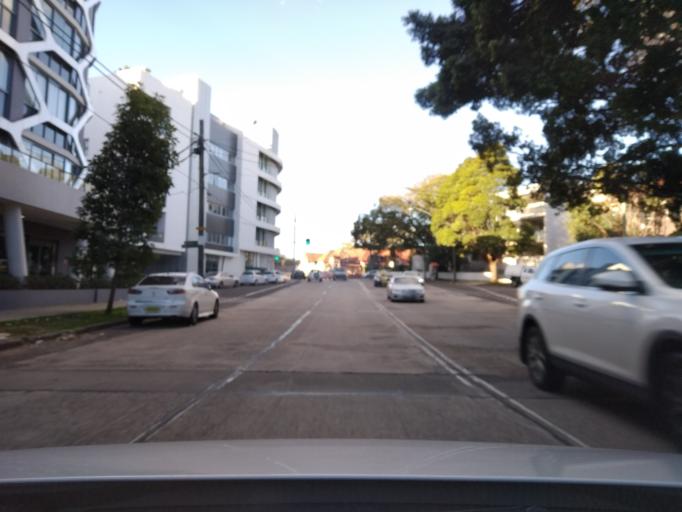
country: AU
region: New South Wales
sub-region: Marrickville
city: Lewisham
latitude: -33.8951
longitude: 151.1435
